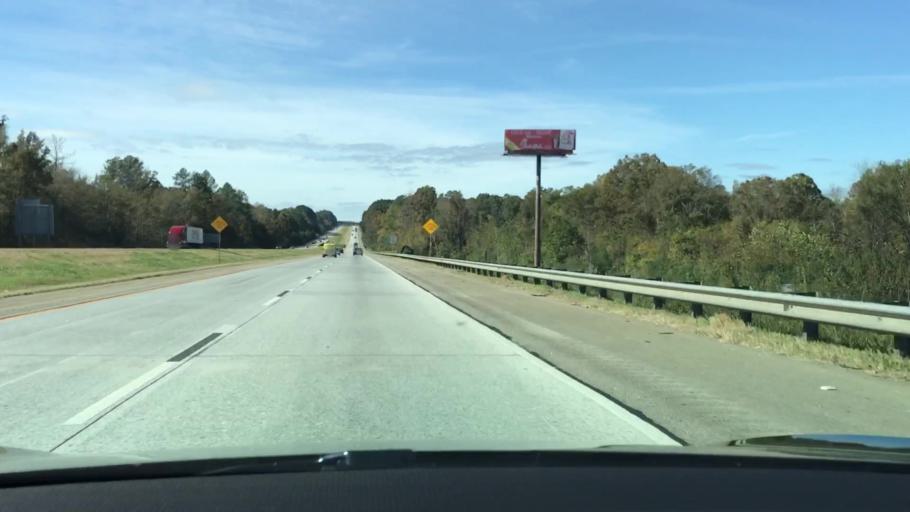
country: US
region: Georgia
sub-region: Greene County
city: Greensboro
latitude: 33.5441
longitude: -83.2177
